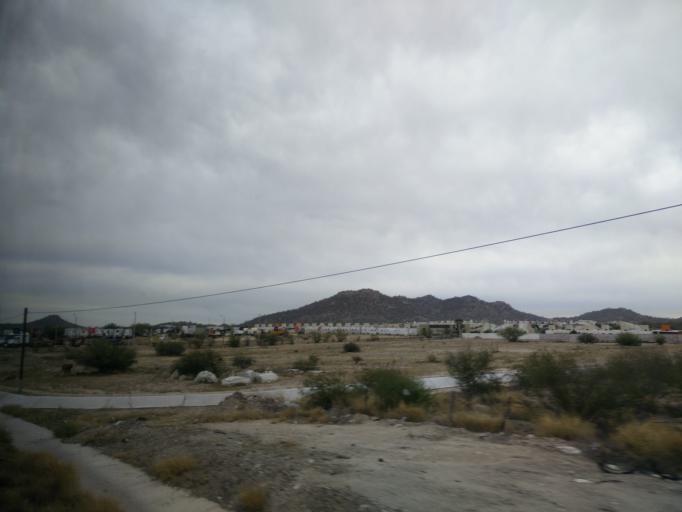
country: MX
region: Sonora
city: Hermosillo
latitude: 28.9959
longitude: -110.9709
